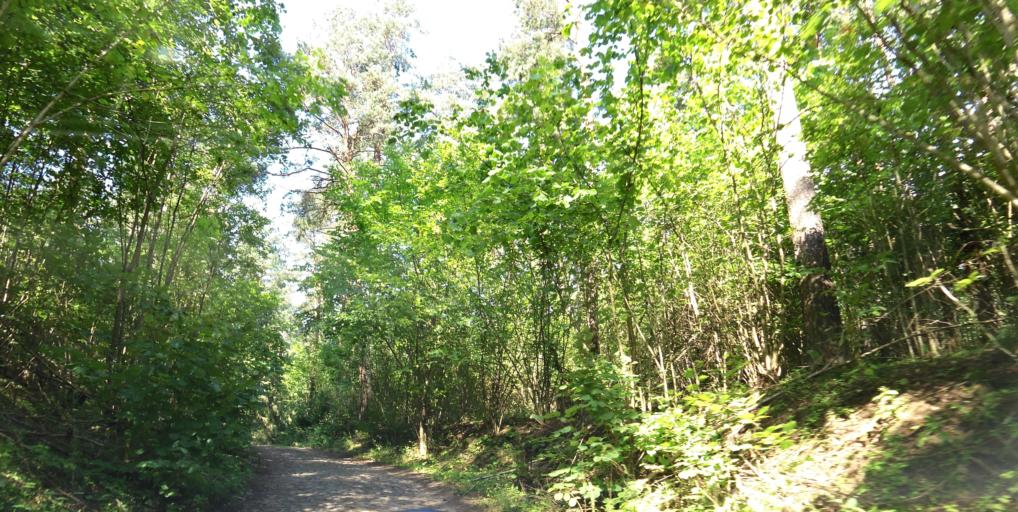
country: LT
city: Grigiskes
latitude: 54.7405
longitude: 25.0311
